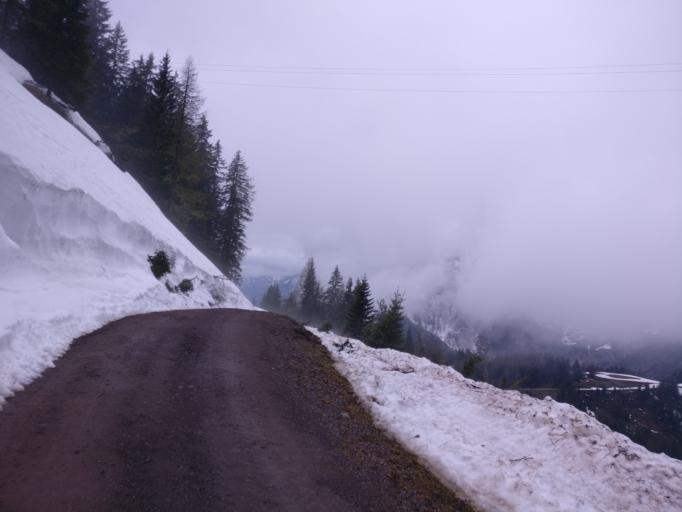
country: AT
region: Salzburg
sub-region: Politischer Bezirk Sankt Johann im Pongau
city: Werfenweng
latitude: 47.4704
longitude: 13.2966
